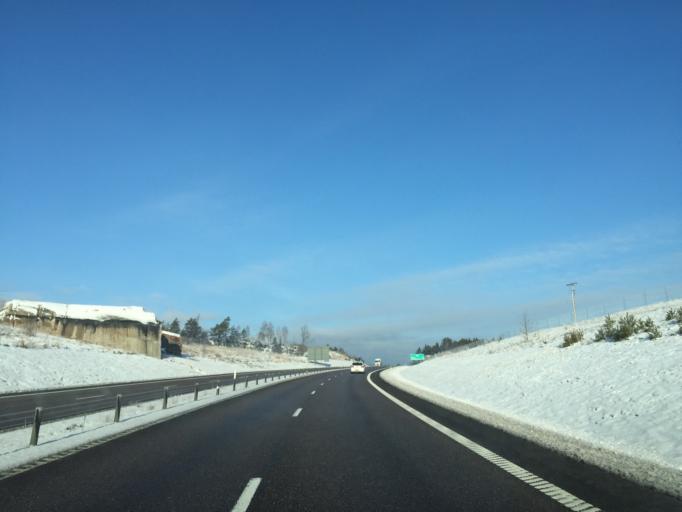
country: SE
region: Vaestra Goetaland
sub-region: Tanums Kommun
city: Tanumshede
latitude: 58.7376
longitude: 11.3051
